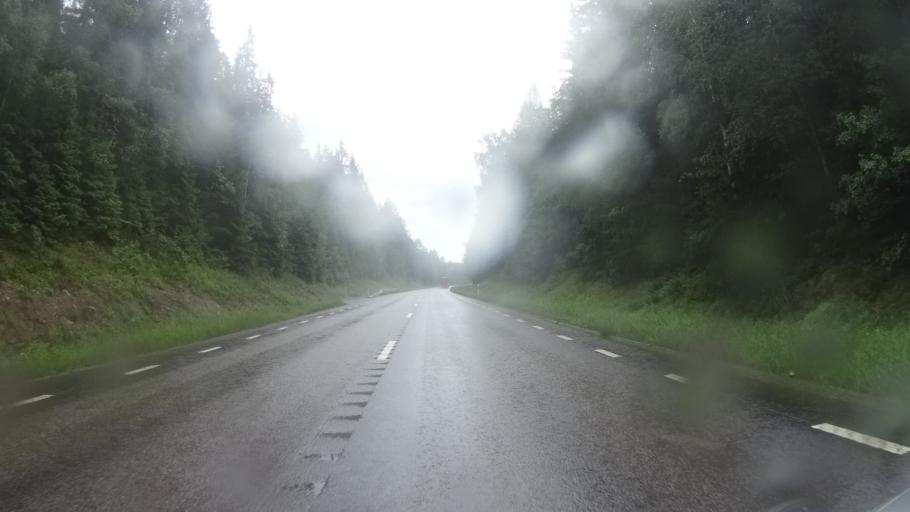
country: SE
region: OEstergoetland
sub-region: Kinda Kommun
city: Kisa
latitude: 57.9521
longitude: 15.6630
